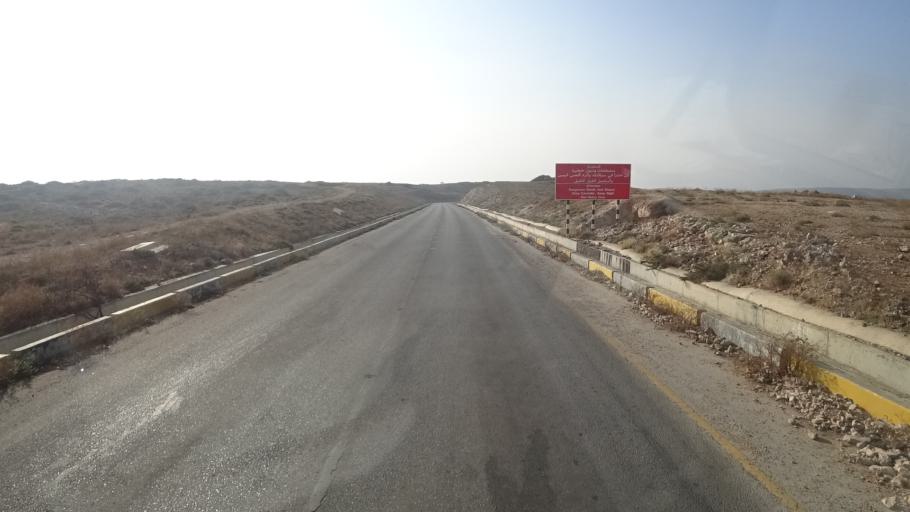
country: YE
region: Al Mahrah
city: Hawf
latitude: 16.7591
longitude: 53.2363
